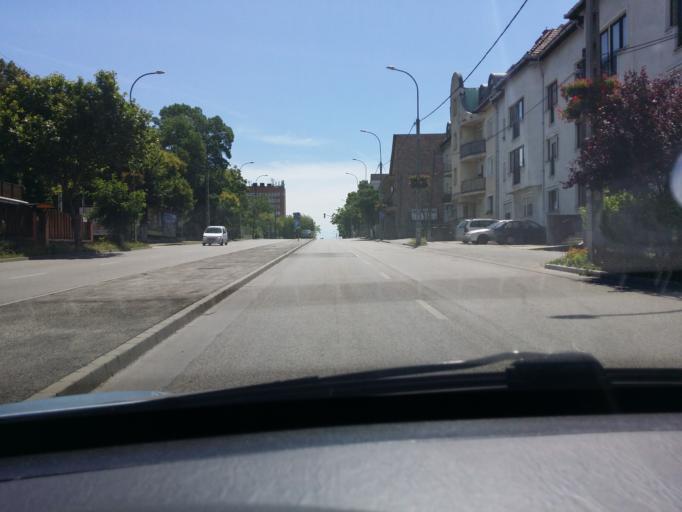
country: HU
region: Budapest
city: Budapest IV. keruelet
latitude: 47.5785
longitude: 19.0912
